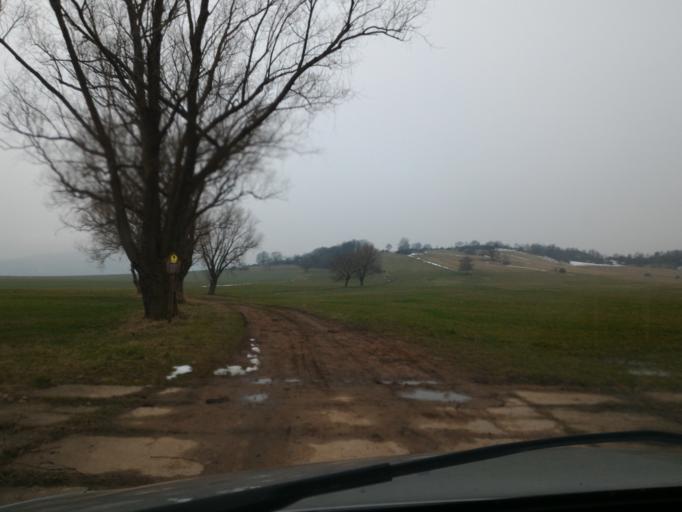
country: DE
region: Saxony
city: Grossschonau
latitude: 50.8994
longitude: 14.6499
